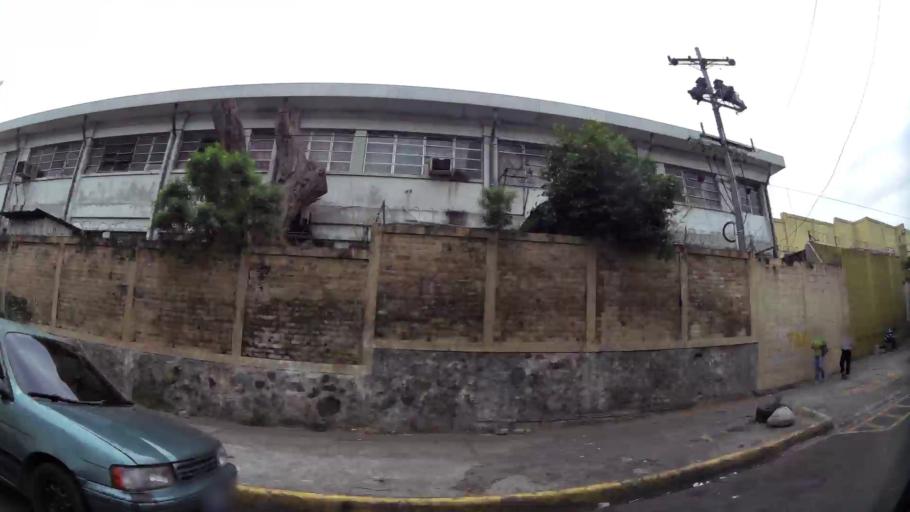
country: SV
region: San Salvador
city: San Salvador
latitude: 13.7015
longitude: -89.2059
